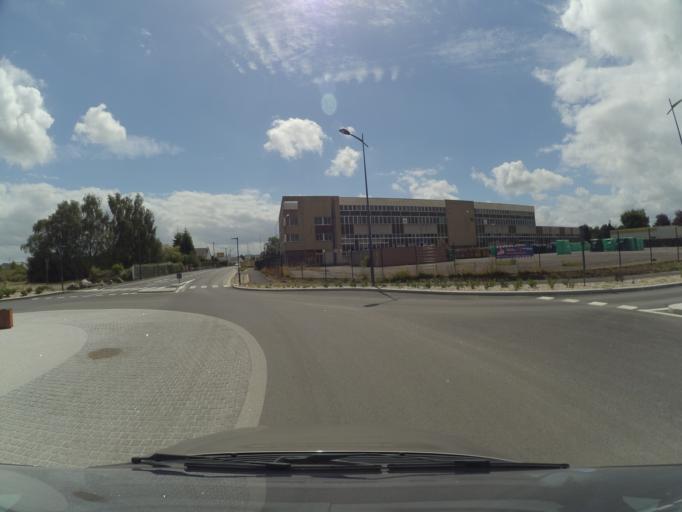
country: FR
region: Brittany
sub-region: Departement des Cotes-d'Armor
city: Saint-Brieuc
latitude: 48.4971
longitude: -2.7654
